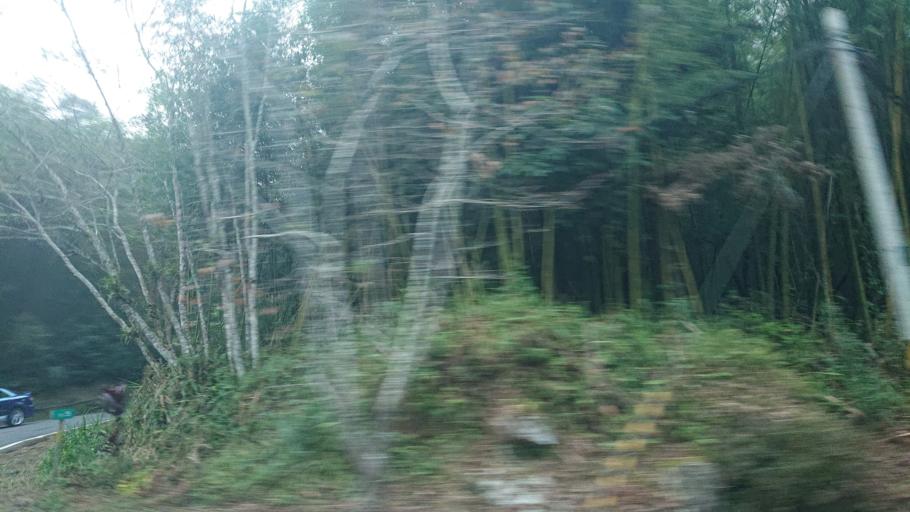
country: TW
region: Taiwan
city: Lugu
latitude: 23.5169
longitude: 120.7020
